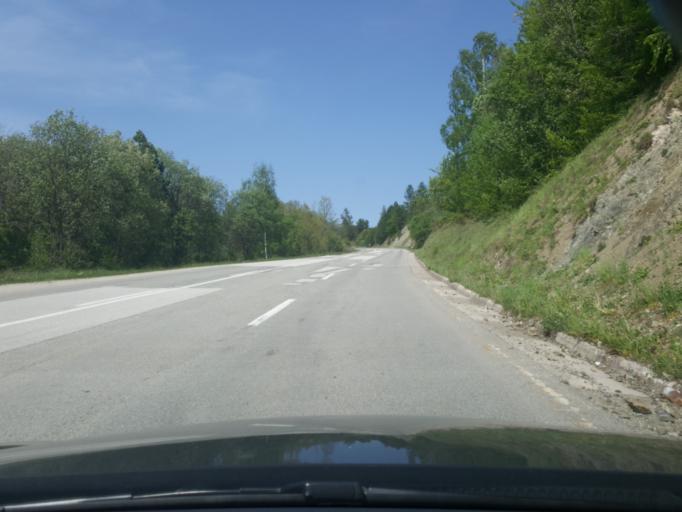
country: RS
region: Central Serbia
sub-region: Zlatiborski Okrug
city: Cajetina
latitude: 43.8129
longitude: 19.6449
